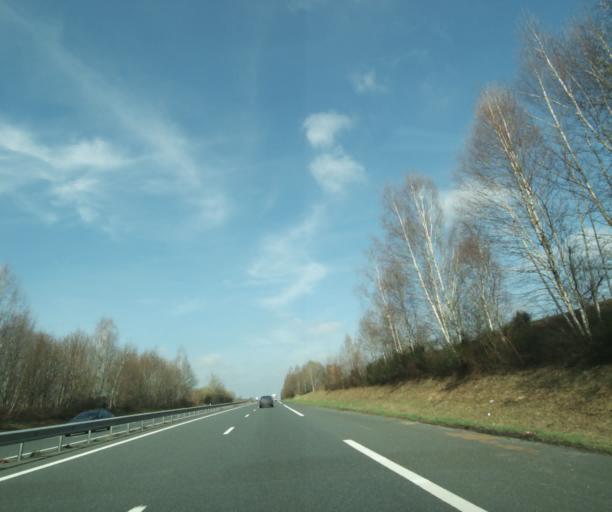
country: FR
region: Limousin
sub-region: Departement de la Haute-Vienne
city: Saint-Sulpice-les-Feuilles
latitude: 46.3879
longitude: 1.4495
